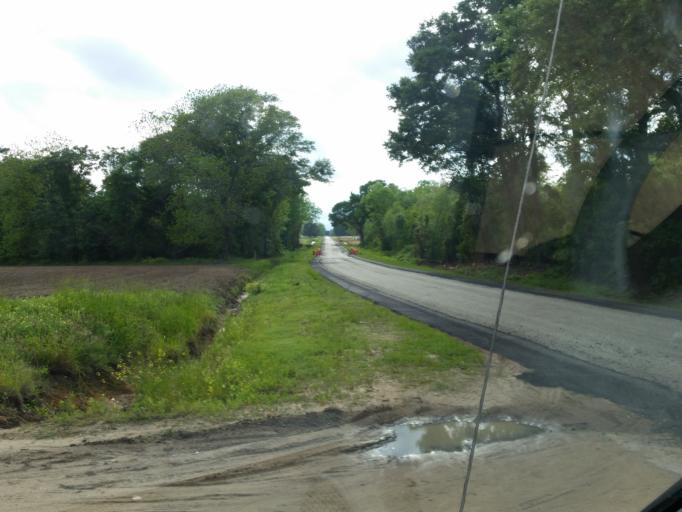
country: US
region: Georgia
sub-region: Dooly County
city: Vienna
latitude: 32.1527
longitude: -83.7756
